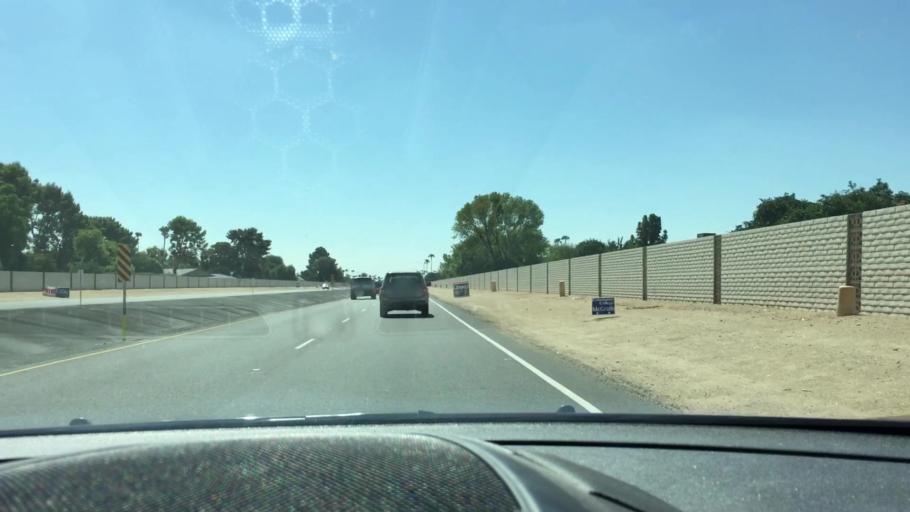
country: US
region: Arizona
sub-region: Maricopa County
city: Sun City
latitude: 33.6507
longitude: -112.2784
